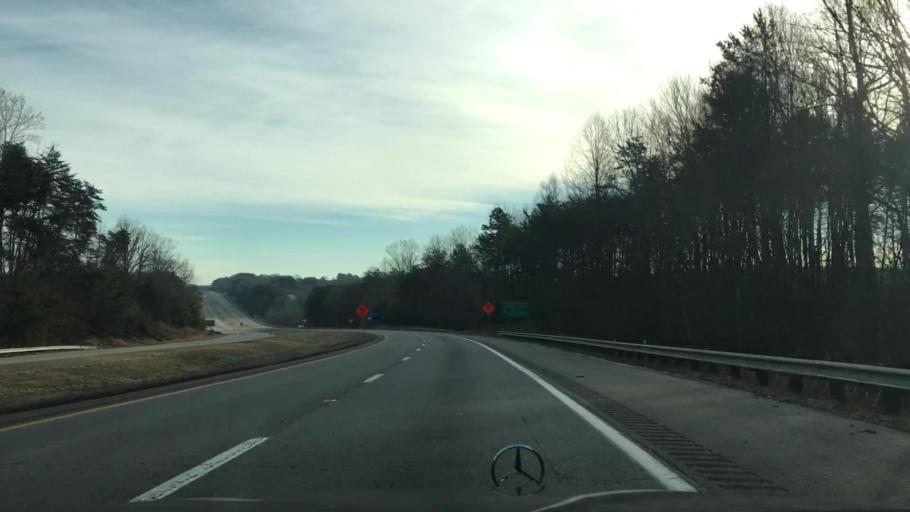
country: US
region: Virginia
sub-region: City of Danville
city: Danville
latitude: 36.5450
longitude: -79.4181
